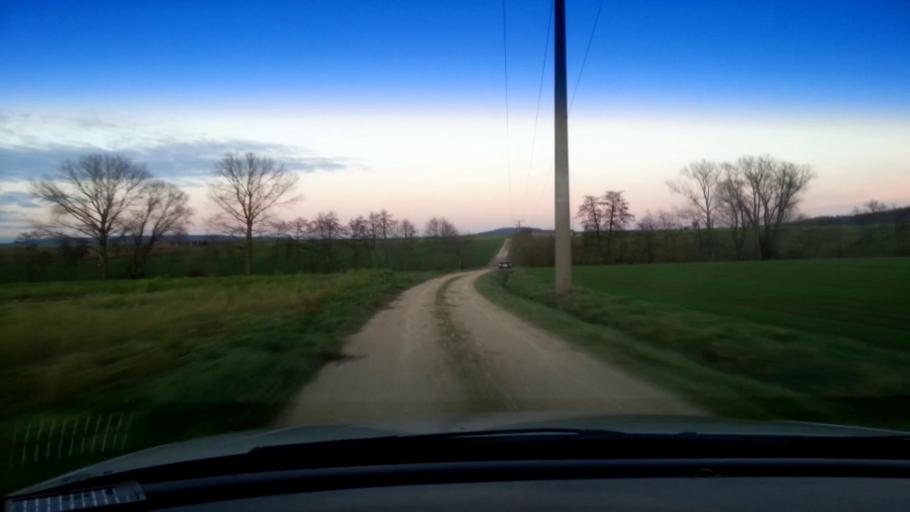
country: DE
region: Bavaria
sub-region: Upper Franconia
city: Litzendorf
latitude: 49.9476
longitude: 11.0055
